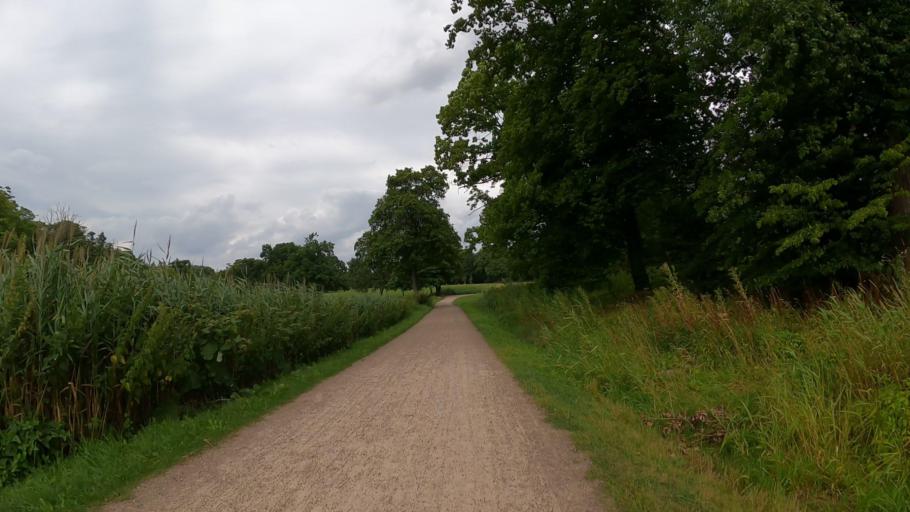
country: DE
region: Hamburg
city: Altona
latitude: 53.5498
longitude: 9.8705
